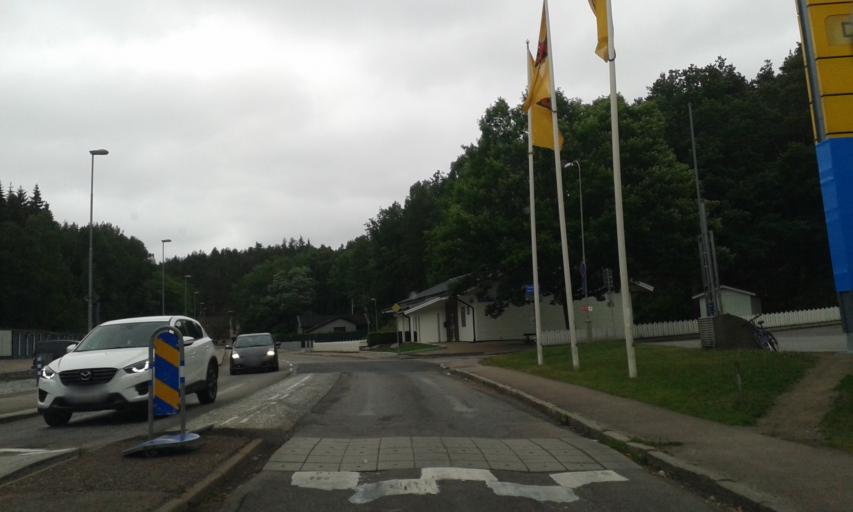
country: SE
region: Vaestra Goetaland
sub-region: Goteborg
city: Eriksbo
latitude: 57.7557
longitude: 12.0274
